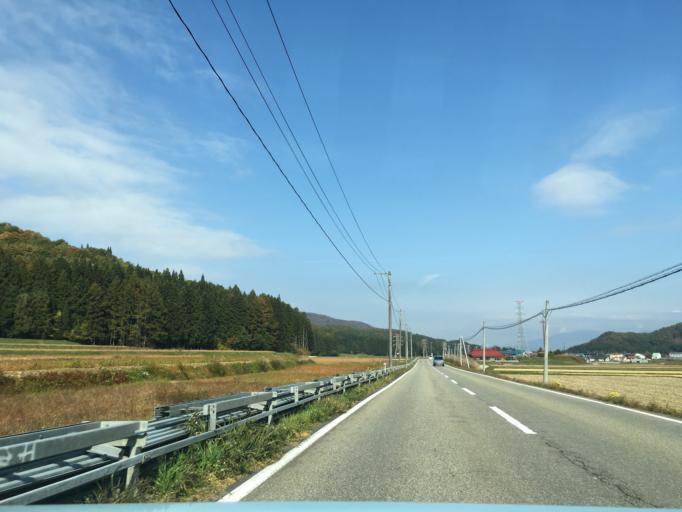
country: JP
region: Fukushima
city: Inawashiro
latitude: 37.4391
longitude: 140.0210
